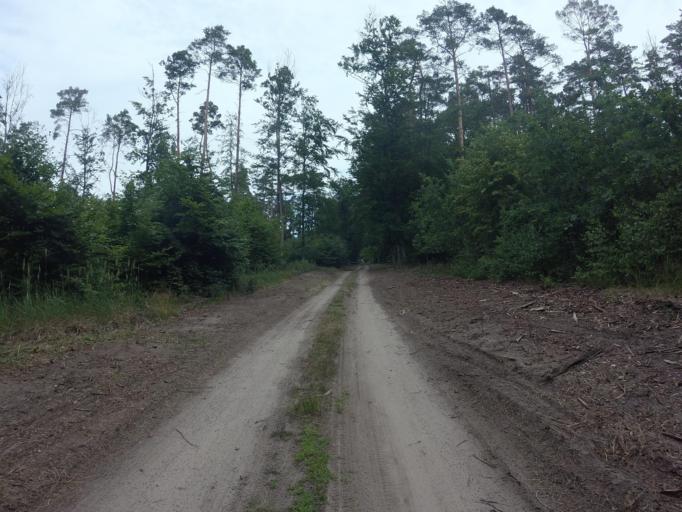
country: PL
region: West Pomeranian Voivodeship
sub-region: Powiat choszczenski
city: Bierzwnik
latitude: 53.0753
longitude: 15.6968
